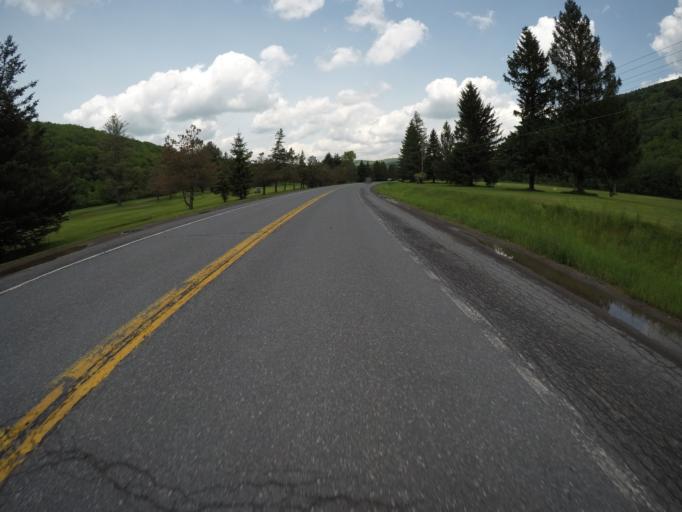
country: US
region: New York
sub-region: Delaware County
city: Stamford
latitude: 42.1730
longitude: -74.6099
